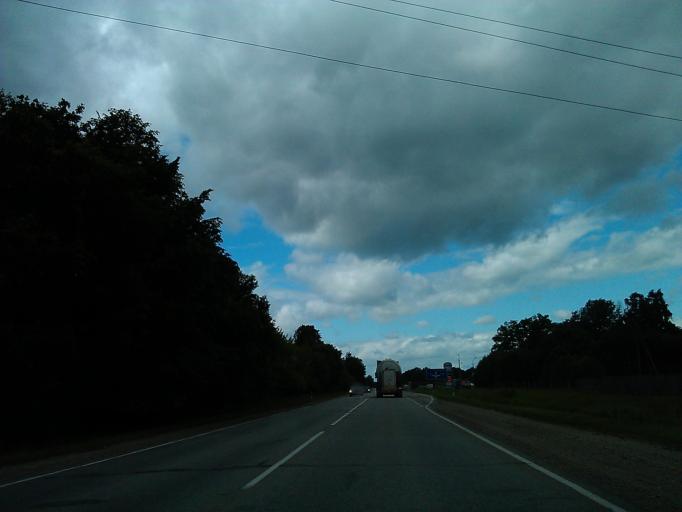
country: LV
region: Tukuma Rajons
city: Tukums
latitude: 56.9315
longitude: 23.2073
